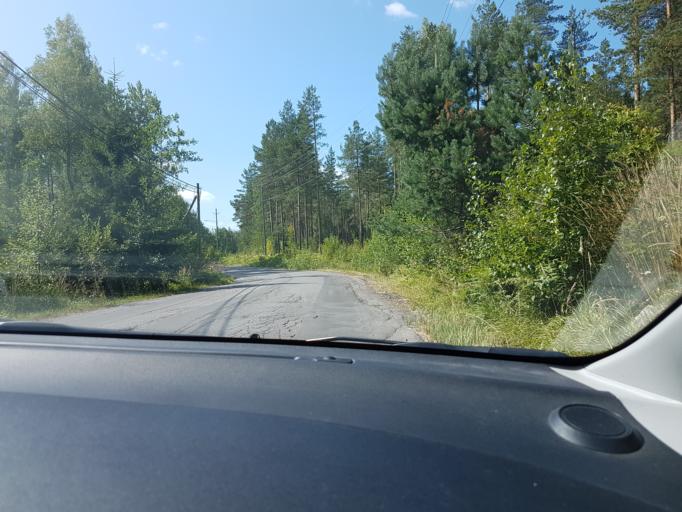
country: FI
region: Uusimaa
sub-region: Helsinki
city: Kilo
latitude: 60.3331
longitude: 24.7809
